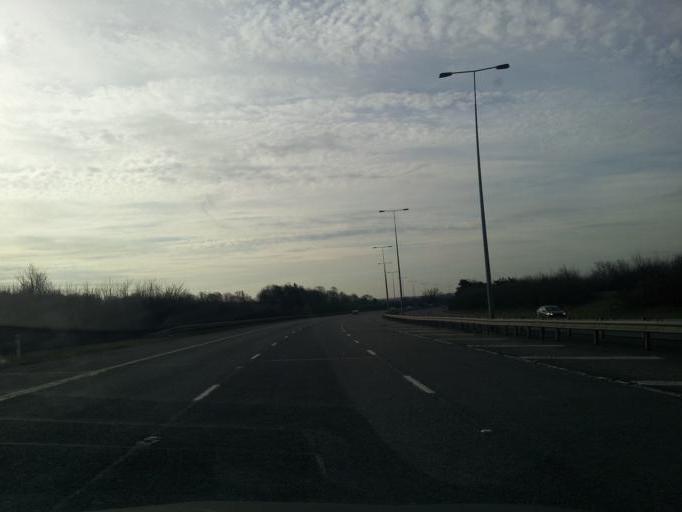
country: GB
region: England
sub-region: Cambridgeshire
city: Great Stukeley
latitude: 52.3746
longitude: -0.2531
